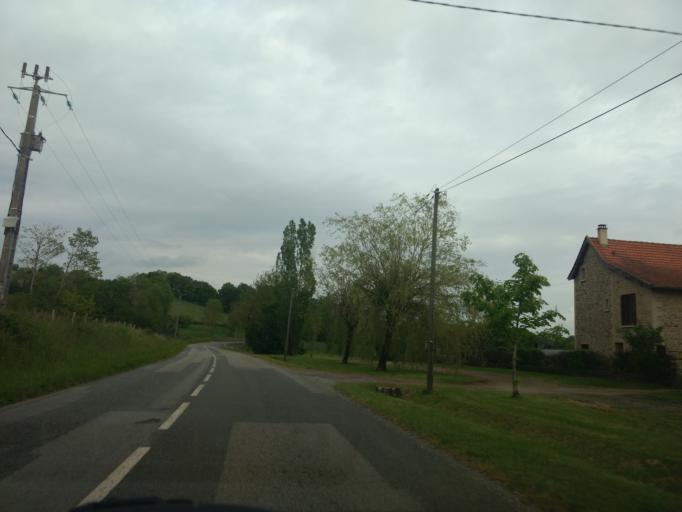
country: FR
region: Midi-Pyrenees
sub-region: Departement de l'Aveyron
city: Montbazens
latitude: 44.4901
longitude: 2.2186
